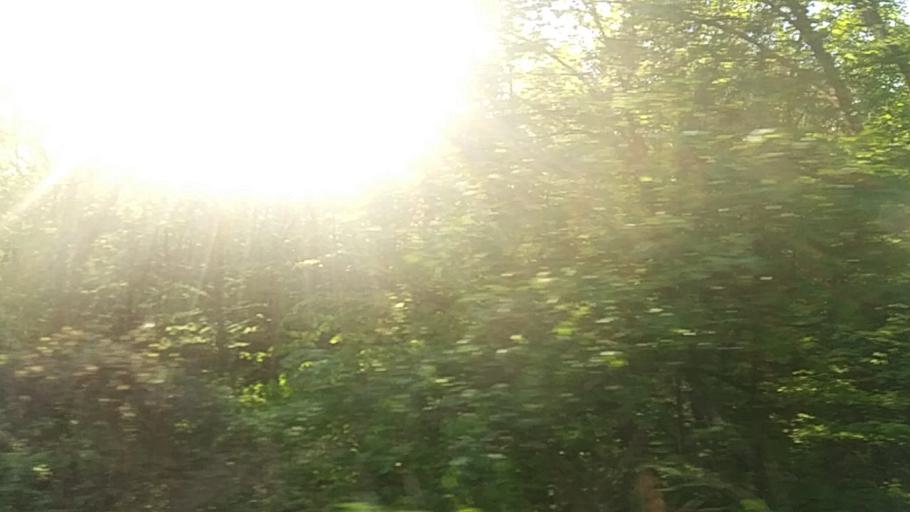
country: US
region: Massachusetts
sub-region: Franklin County
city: Shelburne Falls
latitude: 42.5855
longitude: -72.7446
